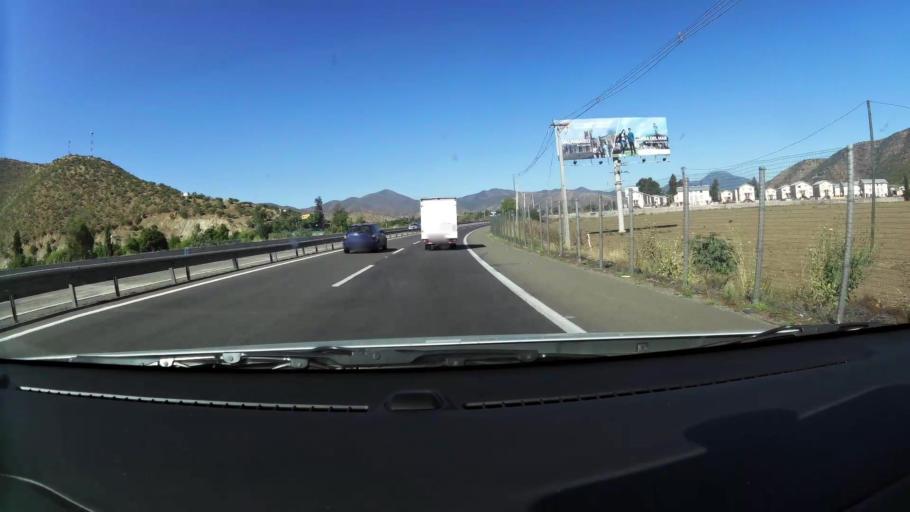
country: CL
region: Santiago Metropolitan
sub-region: Provincia de Chacabuco
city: Lampa
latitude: -33.4087
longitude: -71.1247
